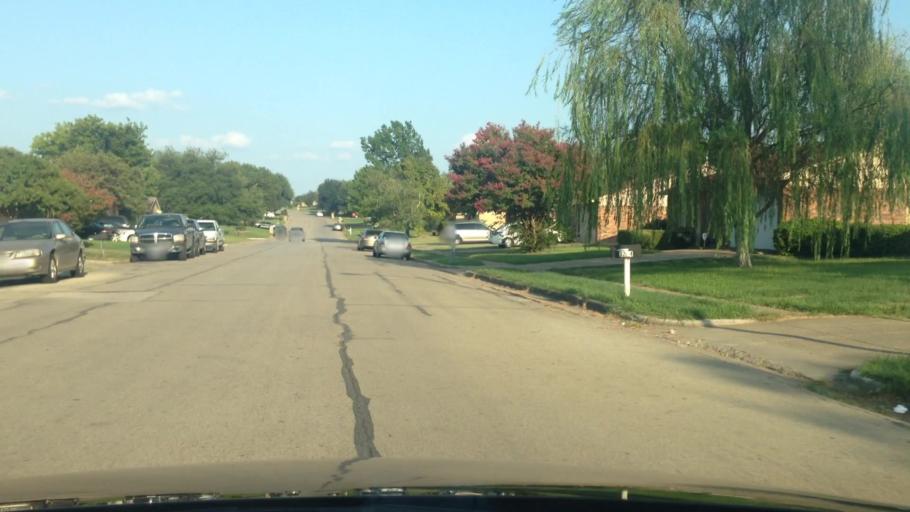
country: US
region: Texas
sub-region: Tarrant County
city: Everman
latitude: 32.6493
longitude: -97.2760
